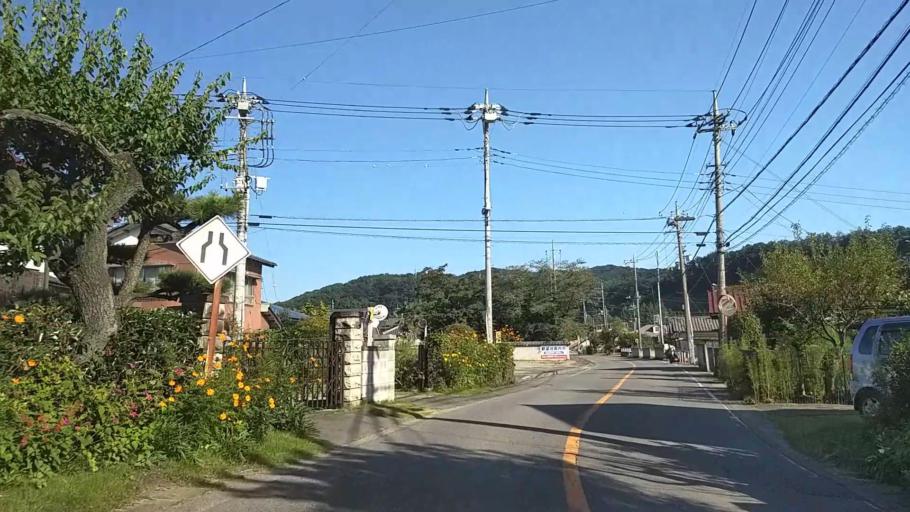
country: JP
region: Gunma
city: Annaka
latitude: 36.3341
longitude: 138.9212
